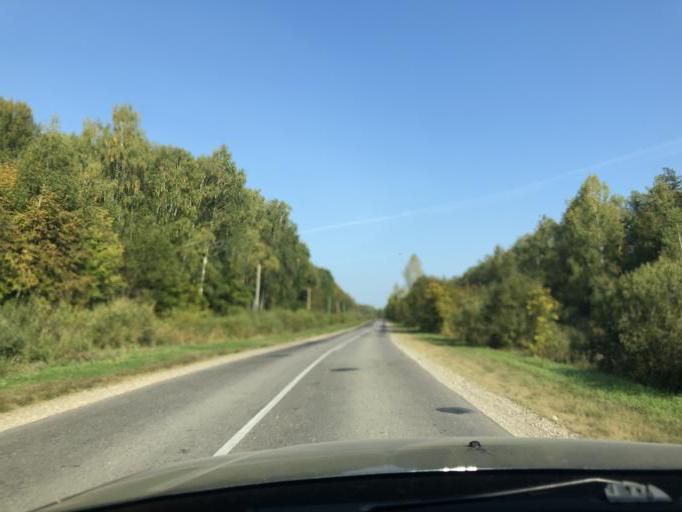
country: RU
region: Tula
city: Leninskiy
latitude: 54.3244
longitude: 37.3976
